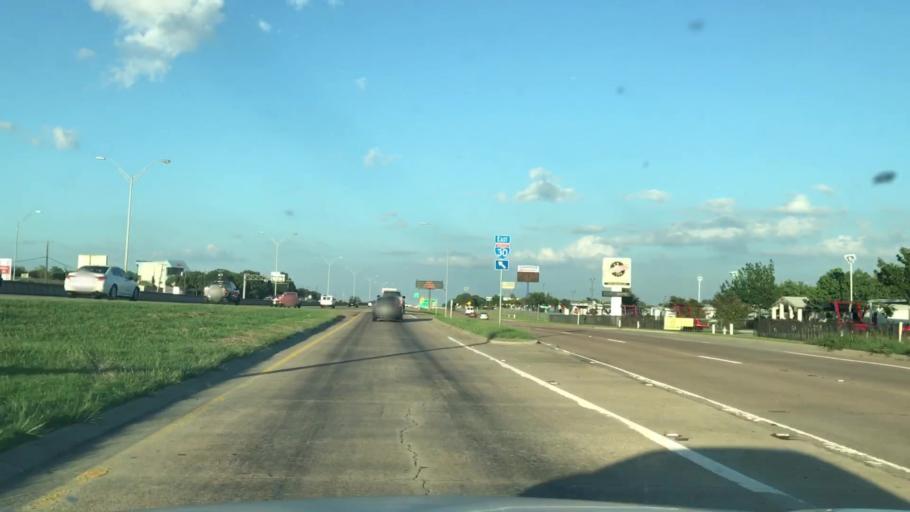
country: US
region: Texas
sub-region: Dallas County
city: Mesquite
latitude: 32.8047
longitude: -96.6657
